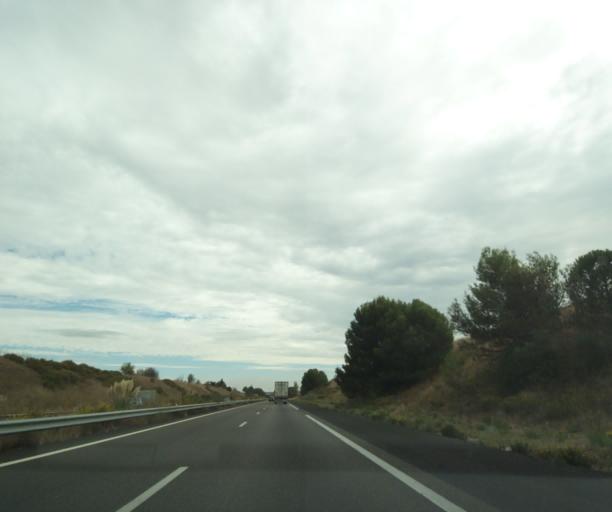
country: FR
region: Languedoc-Roussillon
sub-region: Departement du Gard
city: Garons
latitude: 43.7661
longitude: 4.4218
